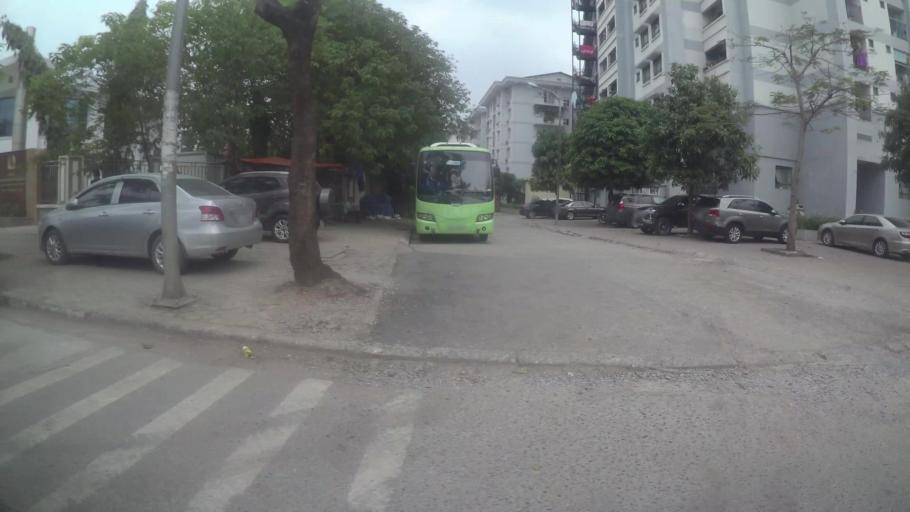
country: VN
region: Ha Noi
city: Cau Dien
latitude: 21.0366
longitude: 105.7713
